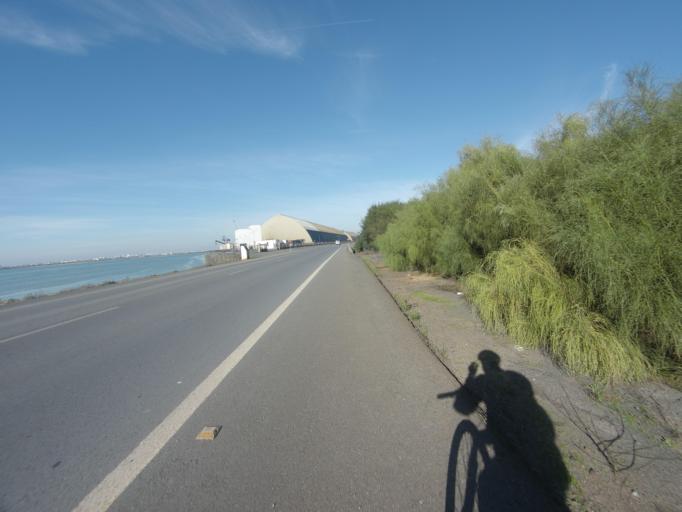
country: ES
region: Andalusia
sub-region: Provincia de Huelva
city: Punta Umbria
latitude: 37.1789
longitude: -6.9189
